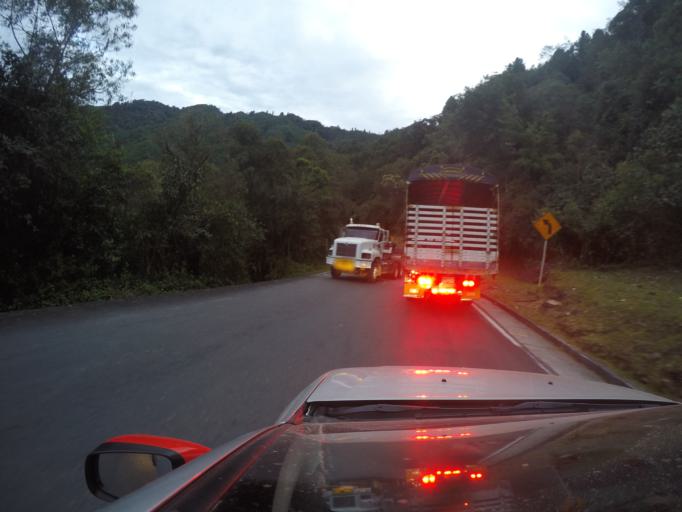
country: CO
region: Tolima
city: Herveo
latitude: 5.1378
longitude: -75.1726
